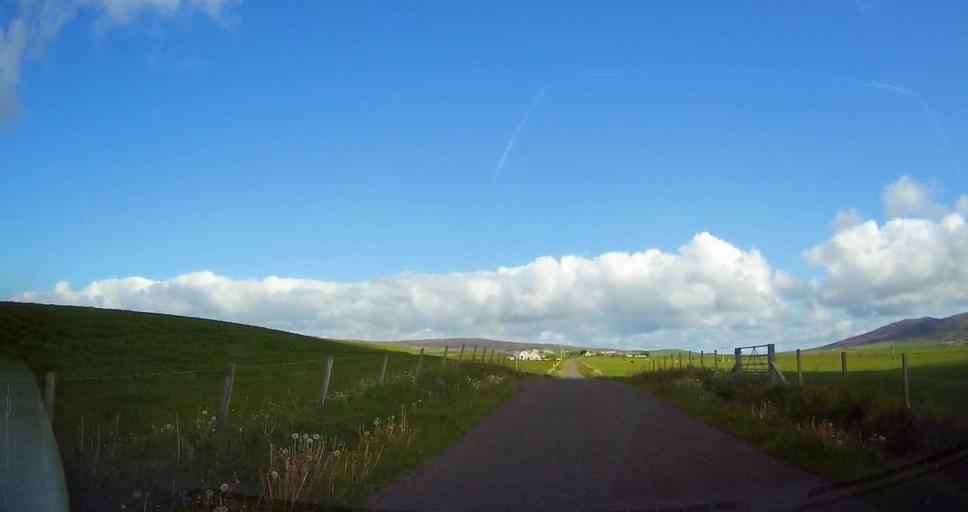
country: GB
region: Scotland
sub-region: Orkney Islands
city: Stromness
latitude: 58.9987
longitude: -3.1686
